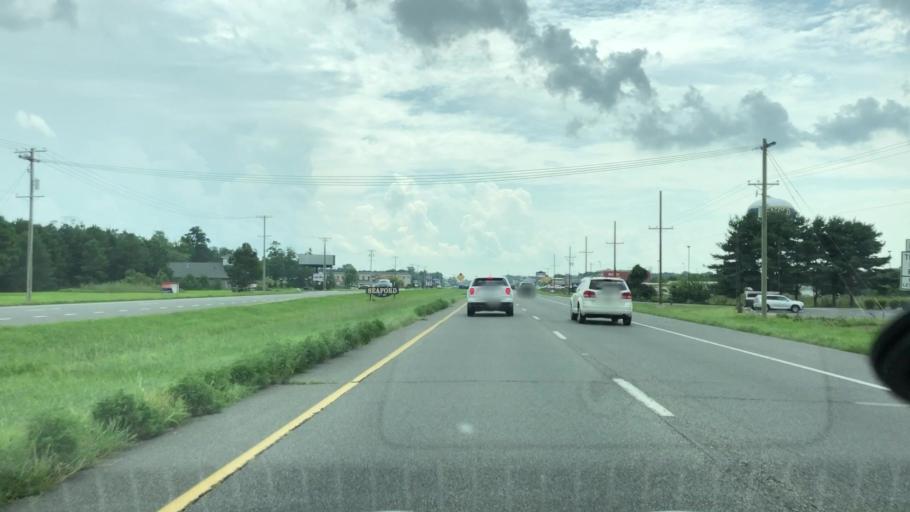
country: US
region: Delaware
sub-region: Sussex County
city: Seaford
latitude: 38.6683
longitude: -75.5931
